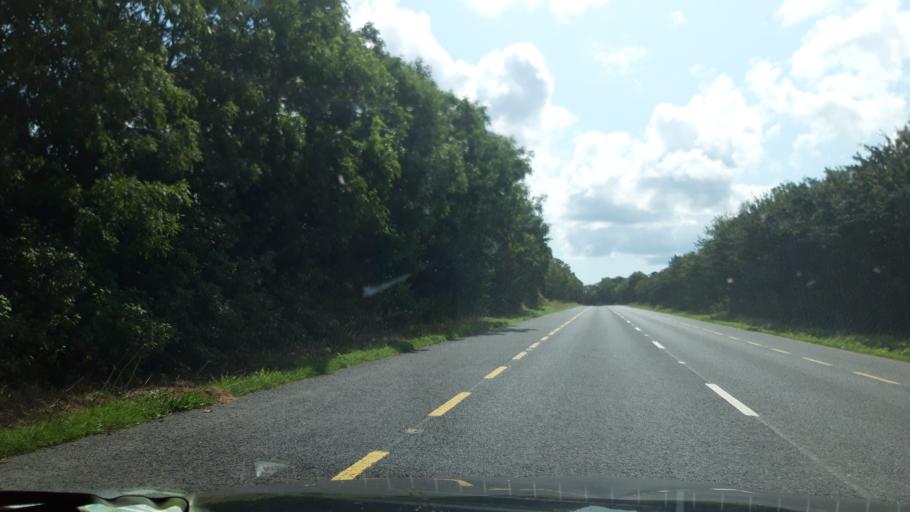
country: IE
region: Munster
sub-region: Waterford
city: Waterford
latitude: 52.2781
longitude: -7.0571
